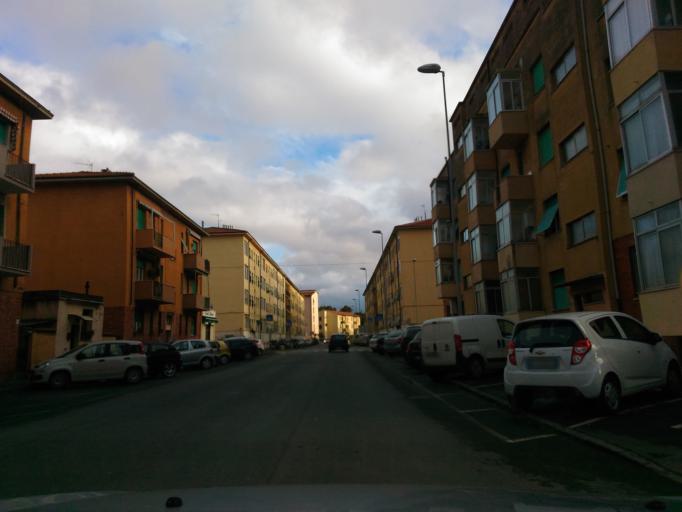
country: IT
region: Tuscany
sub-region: Provincia di Livorno
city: Livorno
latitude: 43.5619
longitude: 10.3314
